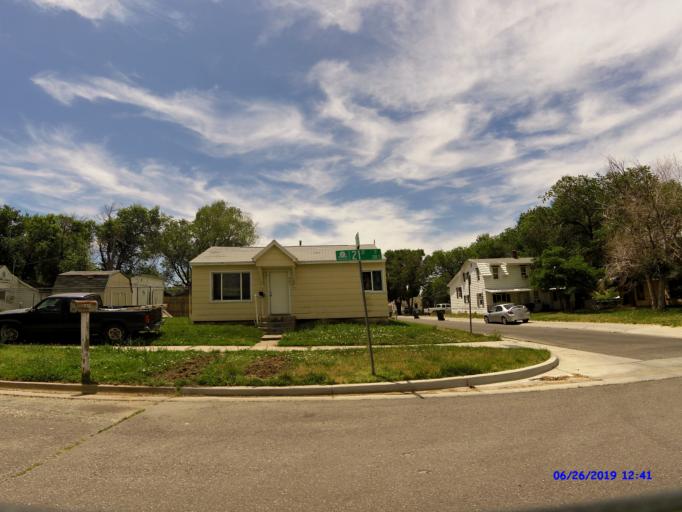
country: US
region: Utah
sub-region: Weber County
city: Ogden
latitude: 41.2288
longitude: -111.9551
